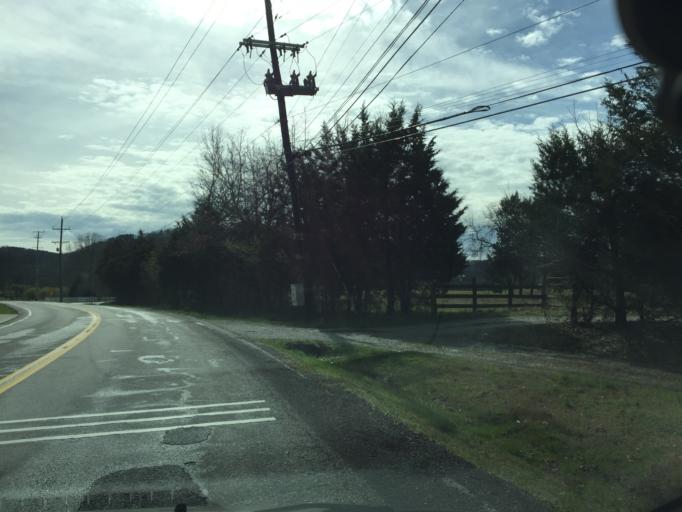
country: US
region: Tennessee
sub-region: Hamilton County
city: Collegedale
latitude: 35.0149
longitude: -85.0921
